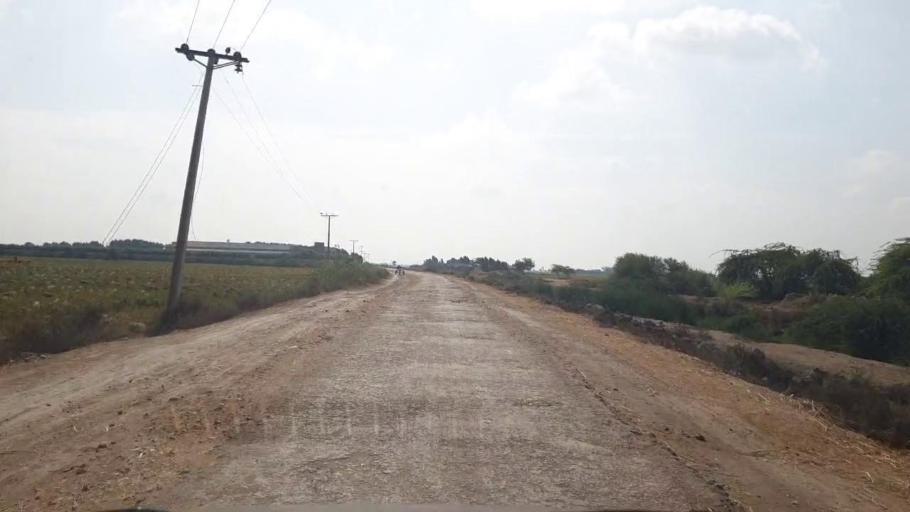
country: PK
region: Sindh
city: Kario
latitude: 24.6393
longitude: 68.5463
